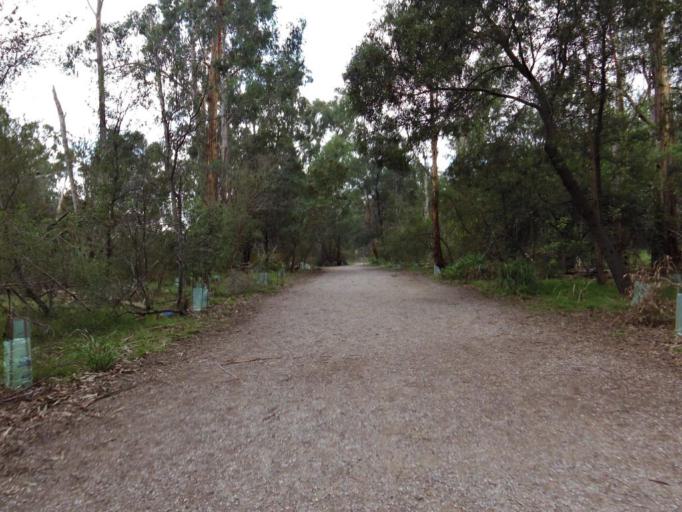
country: AU
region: Victoria
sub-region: Nillumbik
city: North Warrandyte
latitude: -37.7396
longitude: 145.2152
